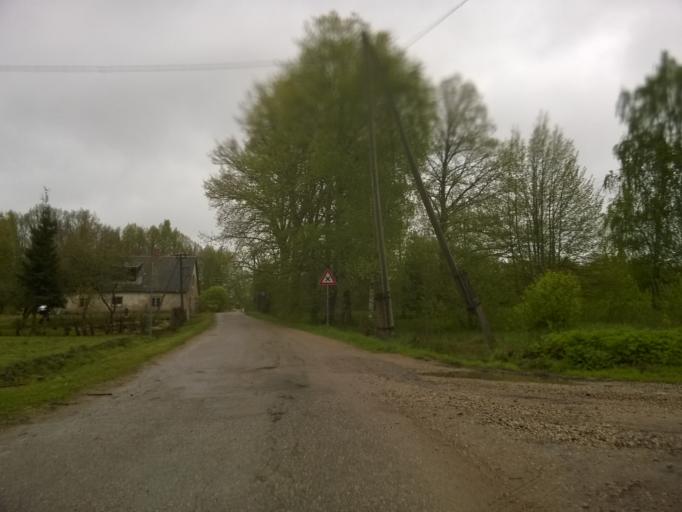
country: LV
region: Amatas Novads
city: Drabesi
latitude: 57.2411
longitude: 25.2097
